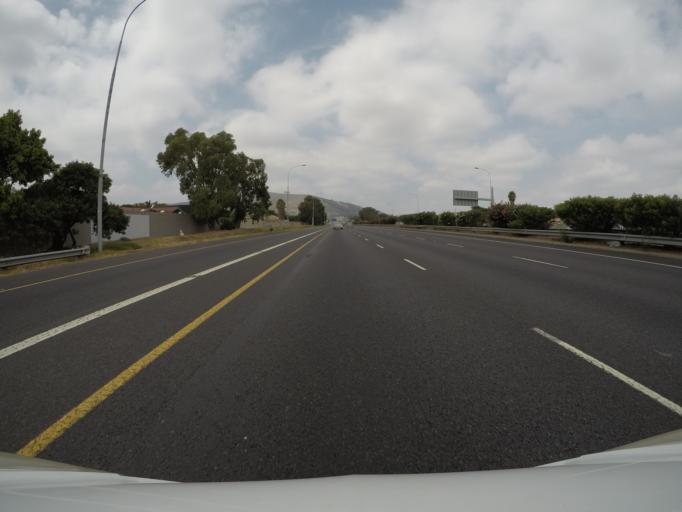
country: ZA
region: Western Cape
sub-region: City of Cape Town
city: Sunset Beach
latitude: -33.8877
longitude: 18.5691
